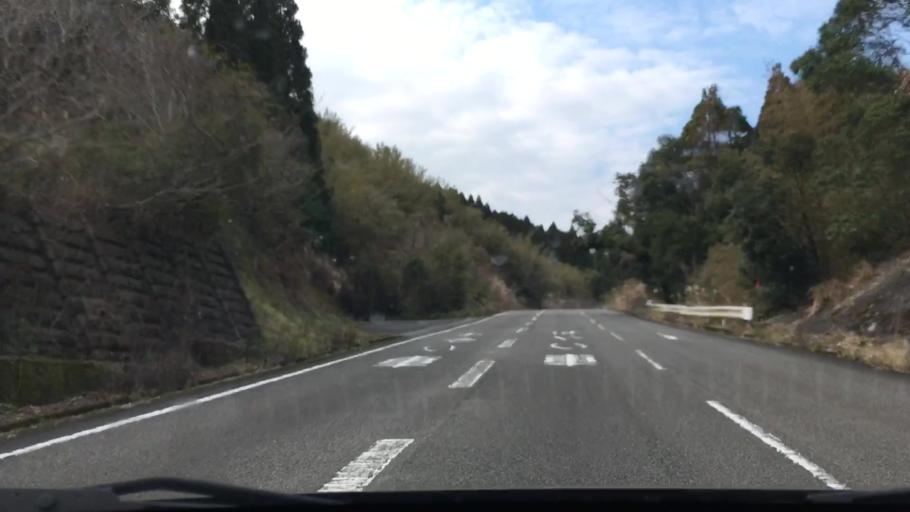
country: JP
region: Miyazaki
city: Nichinan
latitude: 31.6347
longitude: 131.3381
